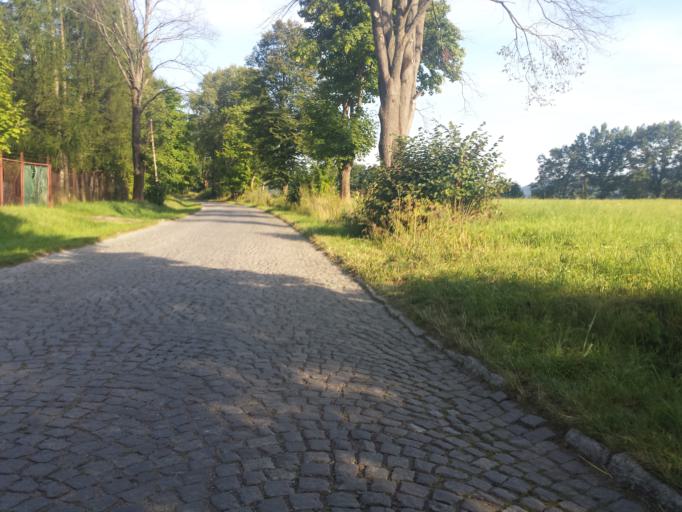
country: PL
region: Subcarpathian Voivodeship
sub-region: Powiat leski
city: Uherce Mineralne
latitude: 49.4451
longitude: 22.3954
